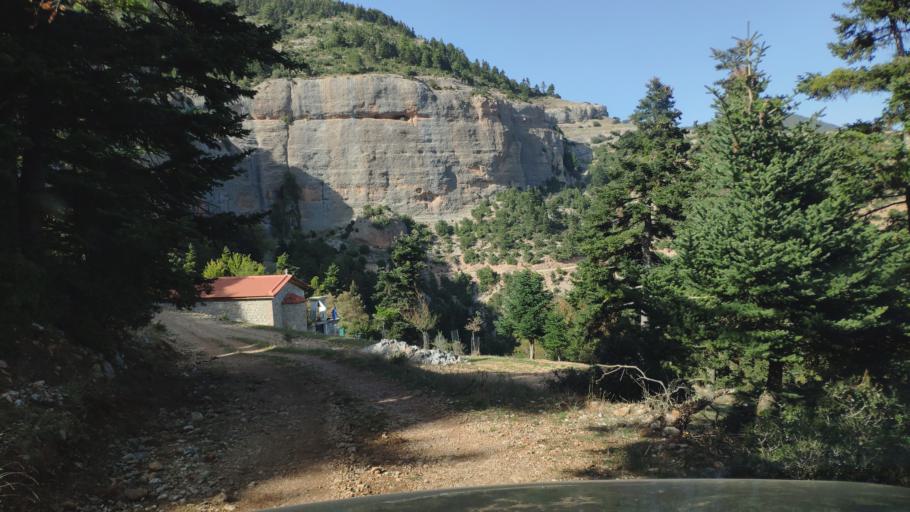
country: GR
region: West Greece
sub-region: Nomos Achaias
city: Aiyira
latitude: 37.9822
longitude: 22.3438
